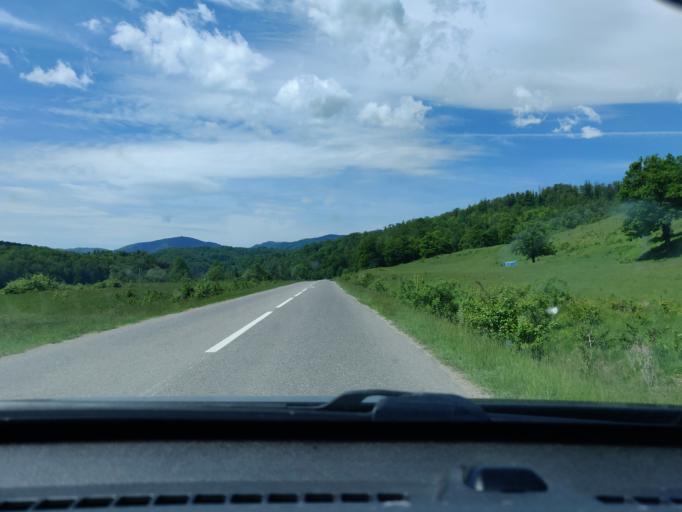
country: RO
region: Vrancea
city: Dragosloveni
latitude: 46.0411
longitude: 26.7169
